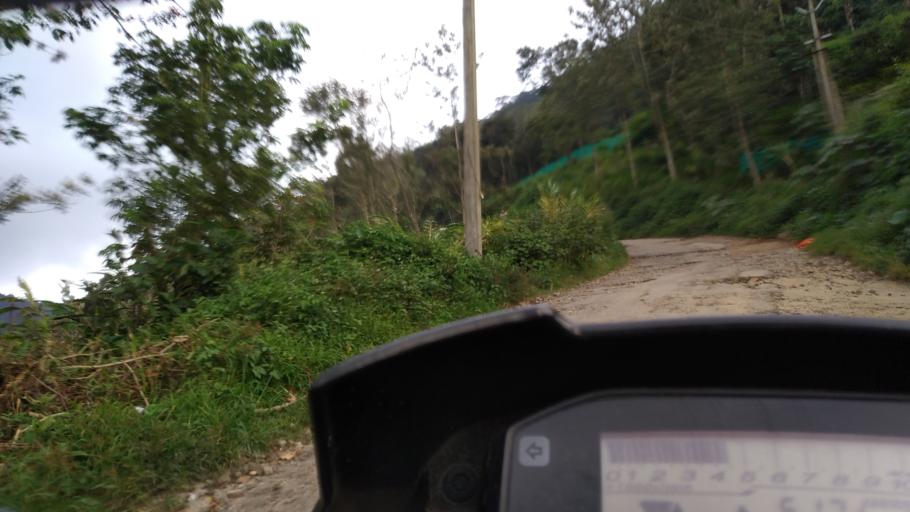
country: IN
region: Tamil Nadu
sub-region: Theni
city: Bodinayakkanur
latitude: 10.0222
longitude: 77.2480
